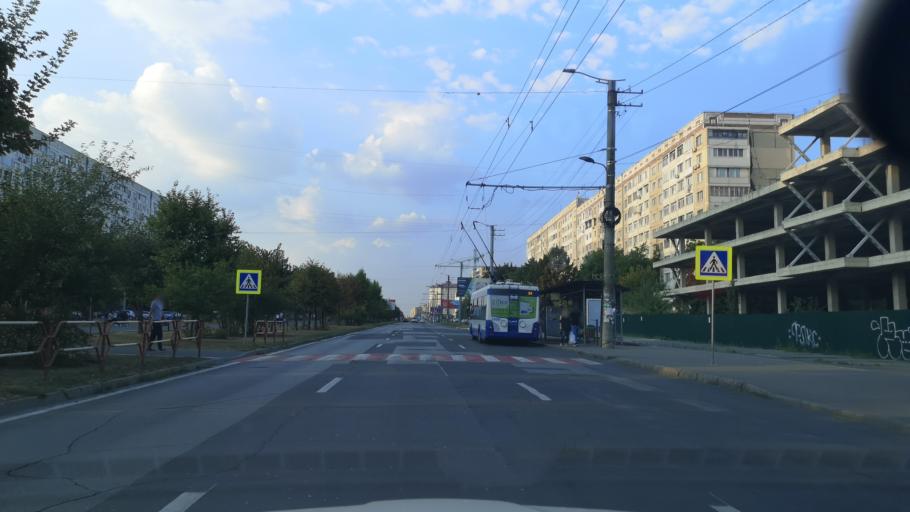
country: MD
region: Chisinau
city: Chisinau
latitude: 47.0404
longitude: 28.8902
